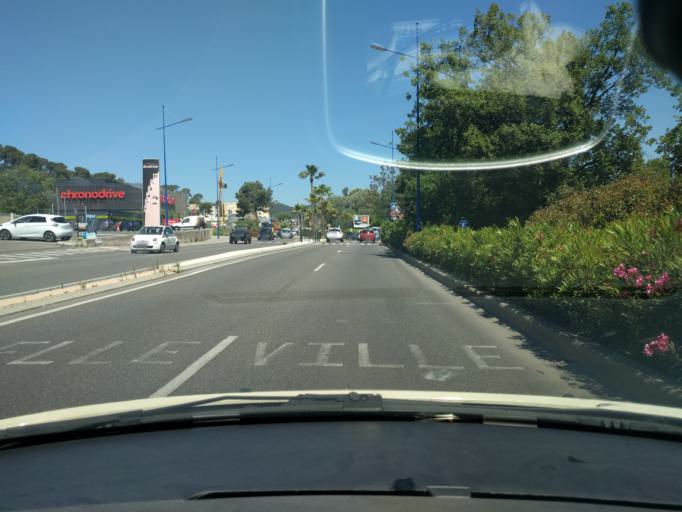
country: FR
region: Provence-Alpes-Cote d'Azur
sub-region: Departement du Var
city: Hyeres
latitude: 43.1040
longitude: 6.1282
